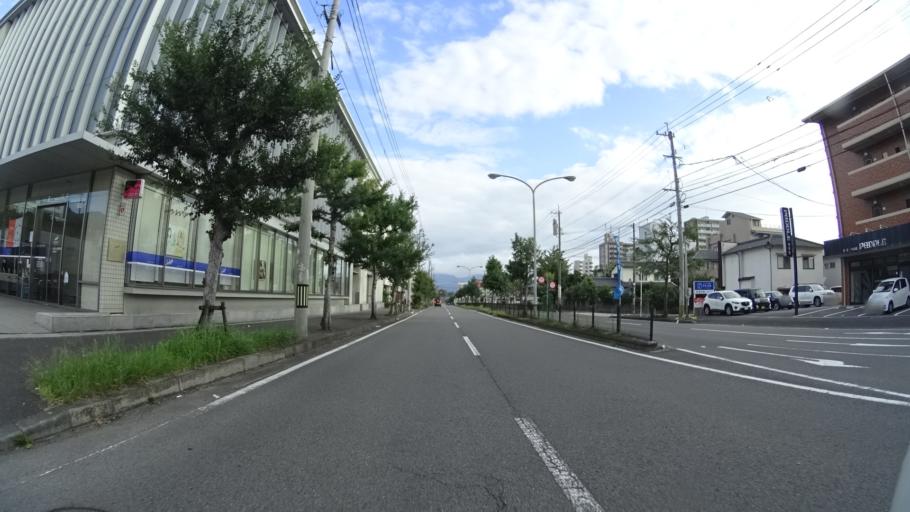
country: JP
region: Oita
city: Beppu
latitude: 33.2995
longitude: 131.4952
